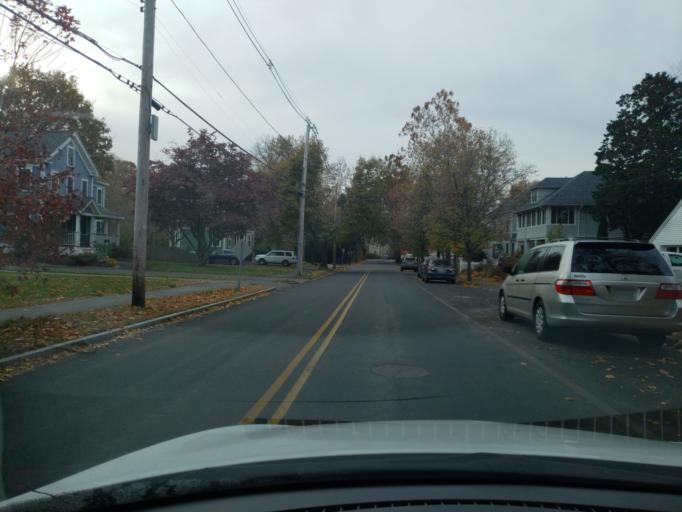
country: US
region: Massachusetts
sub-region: Essex County
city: Andover
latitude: 42.6574
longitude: -71.1359
